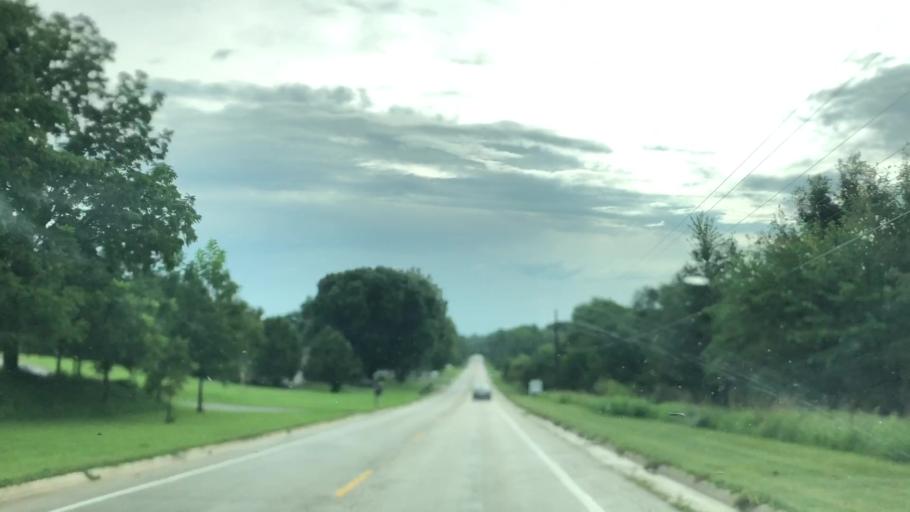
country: US
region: Iowa
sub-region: Marshall County
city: Marshalltown
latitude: 42.0490
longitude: -92.9543
